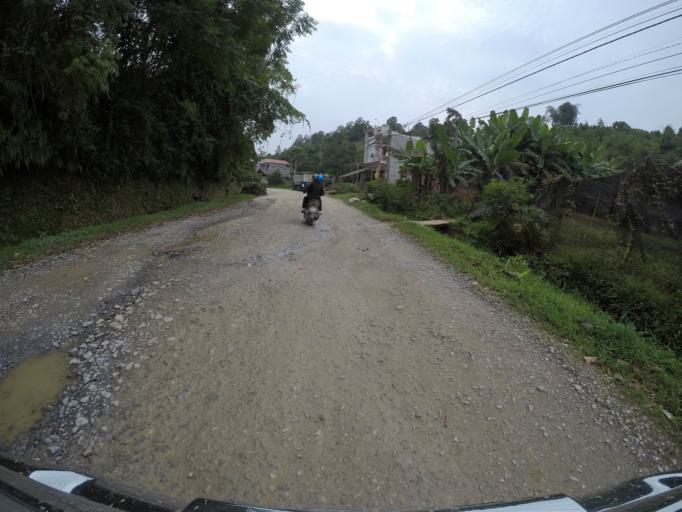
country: VN
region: Yen Bai
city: Co Phuc
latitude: 21.8748
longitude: 104.6532
